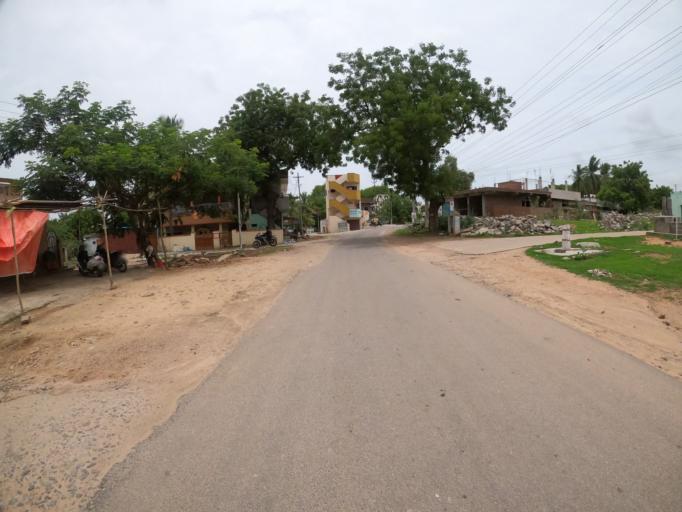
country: IN
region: Telangana
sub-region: Hyderabad
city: Hyderabad
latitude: 17.3387
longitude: 78.3637
